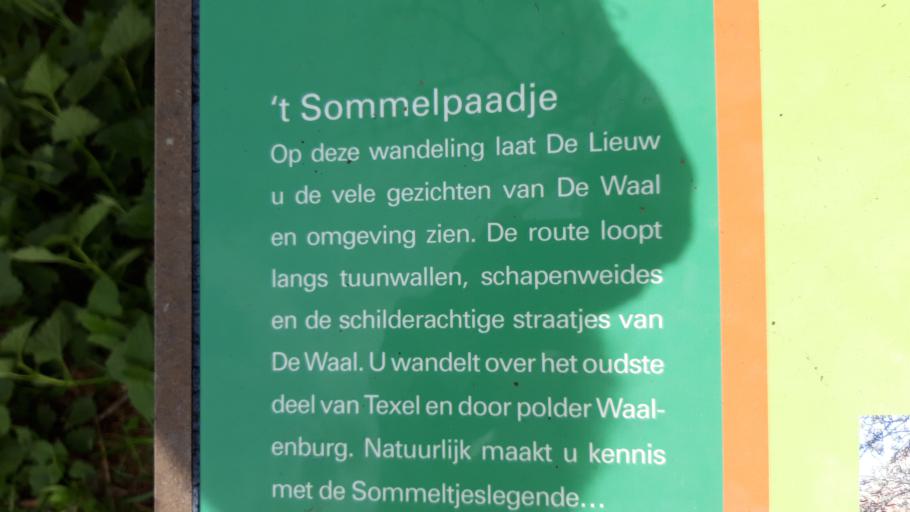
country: NL
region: North Holland
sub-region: Gemeente Texel
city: Den Burg
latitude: 53.0654
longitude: 4.8169
